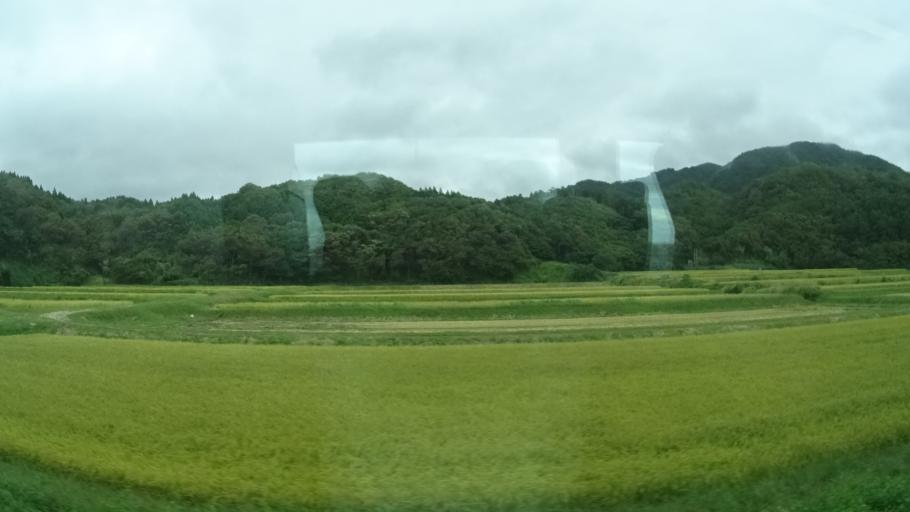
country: JP
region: Niigata
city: Murakami
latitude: 38.2808
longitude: 139.4501
